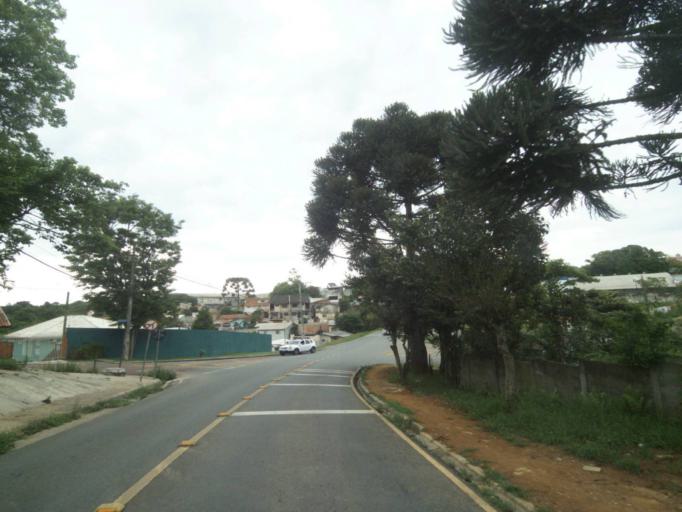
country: BR
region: Parana
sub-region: Curitiba
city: Curitiba
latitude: -25.3968
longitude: -49.2917
